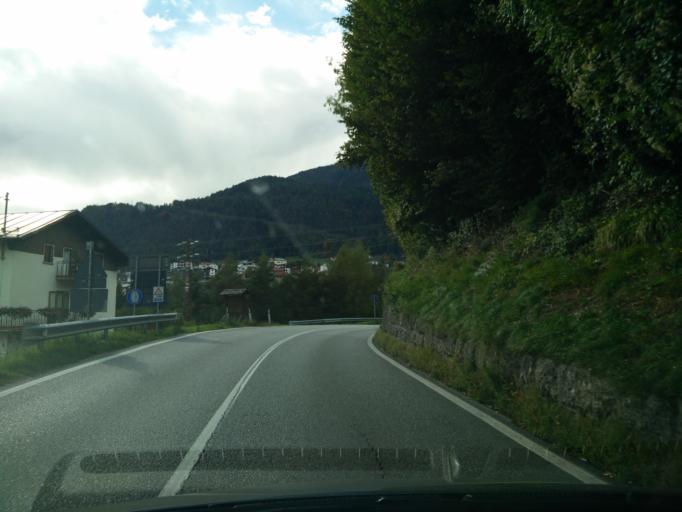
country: IT
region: Veneto
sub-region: Provincia di Belluno
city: Calalzo di Cadore
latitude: 46.4482
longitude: 12.3919
